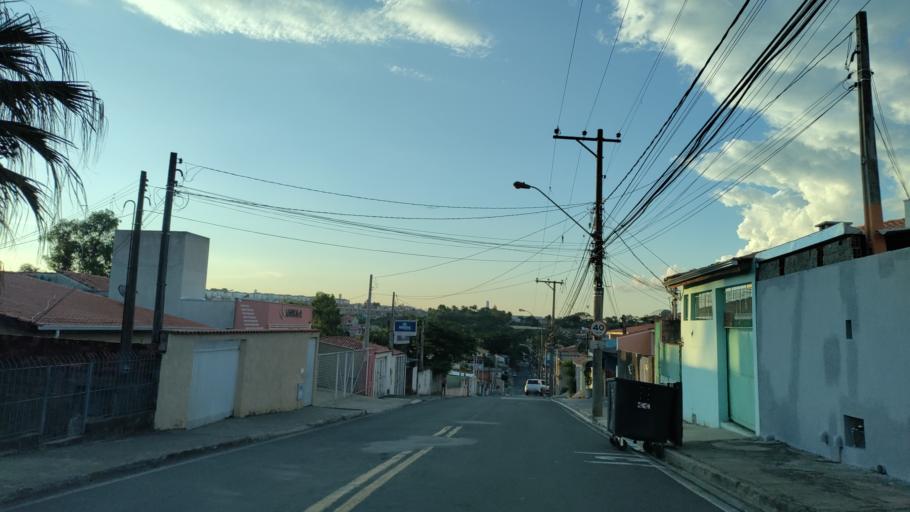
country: BR
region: Sao Paulo
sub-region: Sorocaba
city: Sorocaba
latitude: -23.4724
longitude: -47.4649
